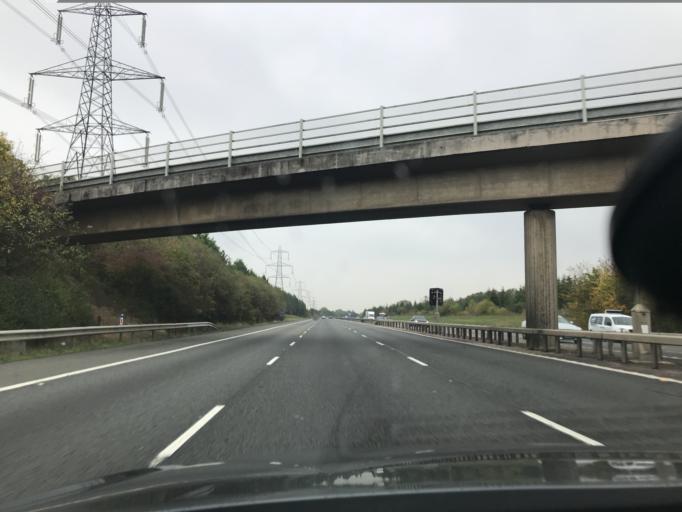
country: GB
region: England
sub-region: Oxfordshire
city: Wheatley
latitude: 51.7996
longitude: -1.0910
